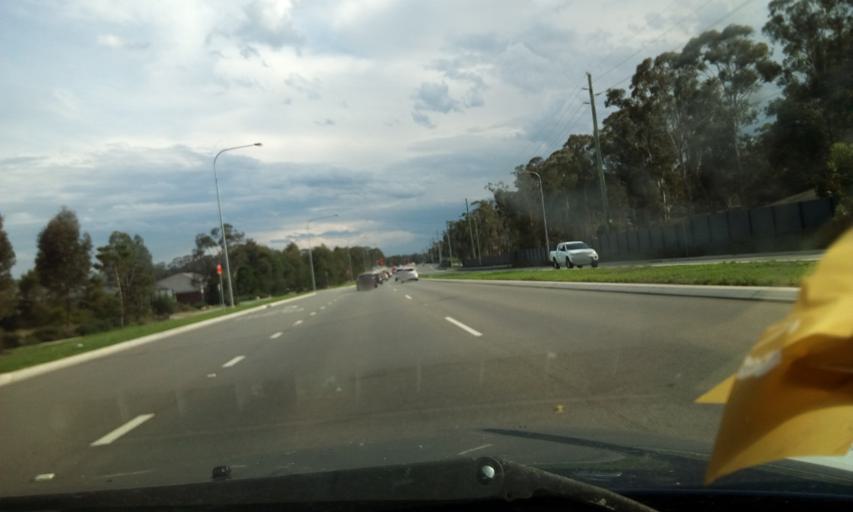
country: AU
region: New South Wales
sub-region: Penrith Municipality
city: Werrington Downs
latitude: -33.7241
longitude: 150.7218
